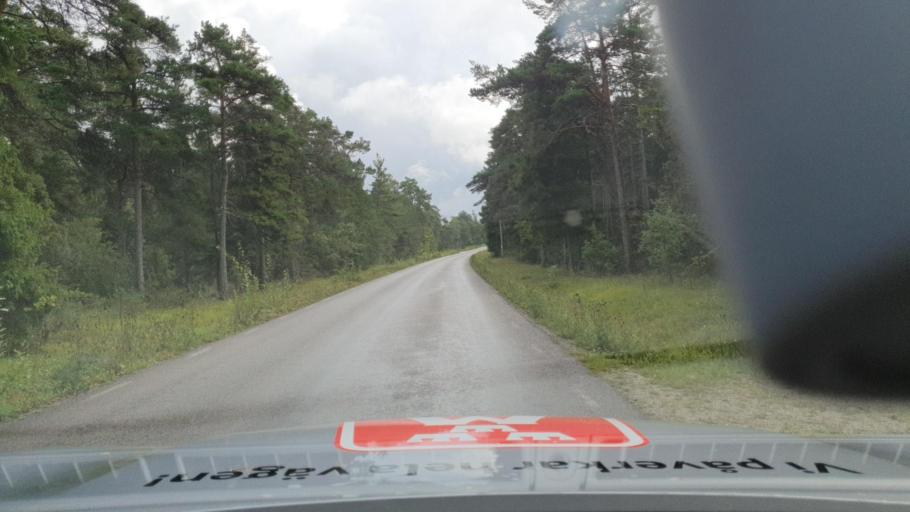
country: SE
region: Gotland
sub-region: Gotland
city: Slite
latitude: 57.7274
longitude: 18.7484
